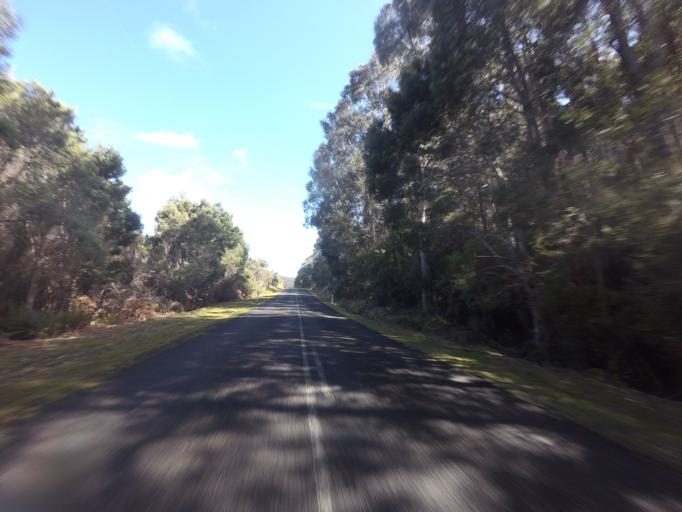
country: AU
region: Tasmania
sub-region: Derwent Valley
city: New Norfolk
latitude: -42.7598
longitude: 146.5307
